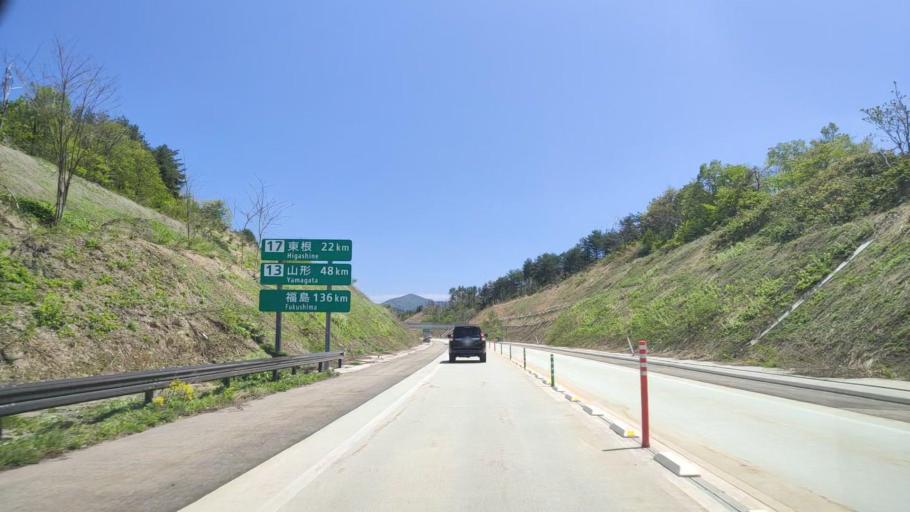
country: JP
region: Yamagata
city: Obanazawa
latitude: 38.5901
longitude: 140.3891
